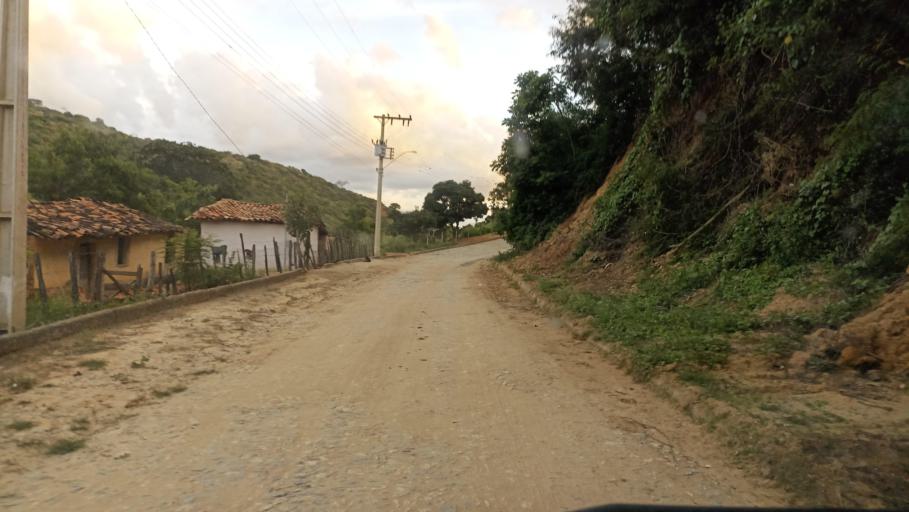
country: BR
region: Minas Gerais
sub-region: Almenara
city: Almenara
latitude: -16.5216
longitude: -40.4416
